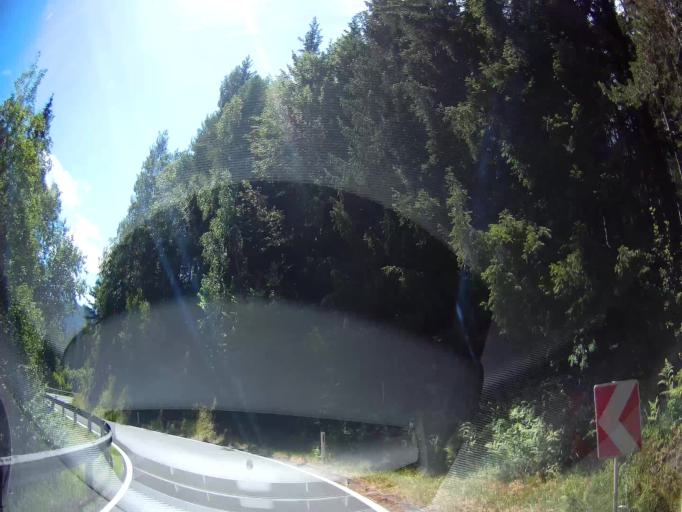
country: AT
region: Carinthia
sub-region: Politischer Bezirk Sankt Veit an der Glan
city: Glodnitz
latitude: 46.9159
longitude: 14.0767
